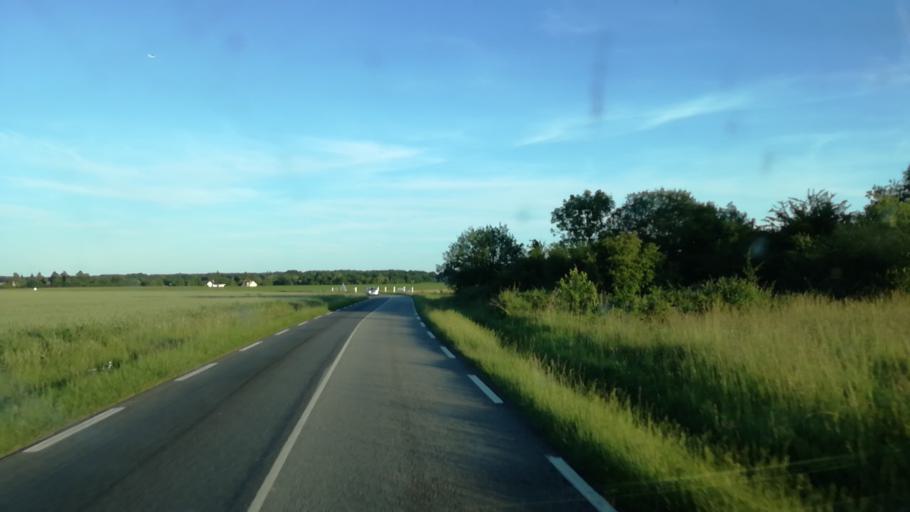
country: FR
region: Ile-de-France
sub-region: Departement des Yvelines
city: Dampierre-en-Yvelines
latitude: 48.7263
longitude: 1.9873
